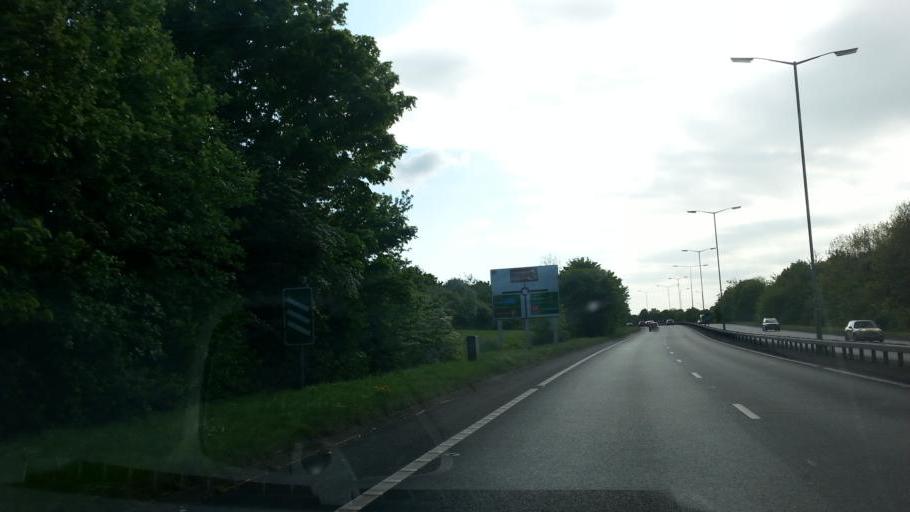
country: GB
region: England
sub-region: Peterborough
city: Peterborough
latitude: 52.5657
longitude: -0.2797
